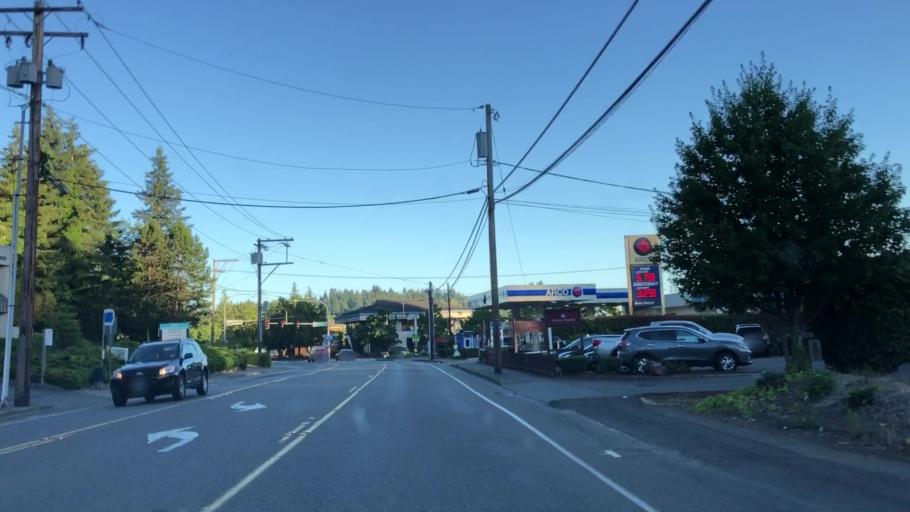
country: US
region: Washington
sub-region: King County
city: Bothell
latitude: 47.7668
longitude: -122.2104
